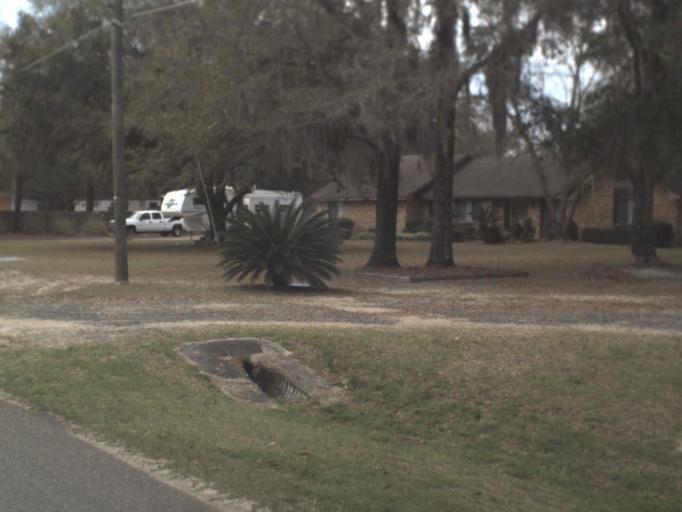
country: US
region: Florida
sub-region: Liberty County
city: Bristol
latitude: 30.4374
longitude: -84.9741
